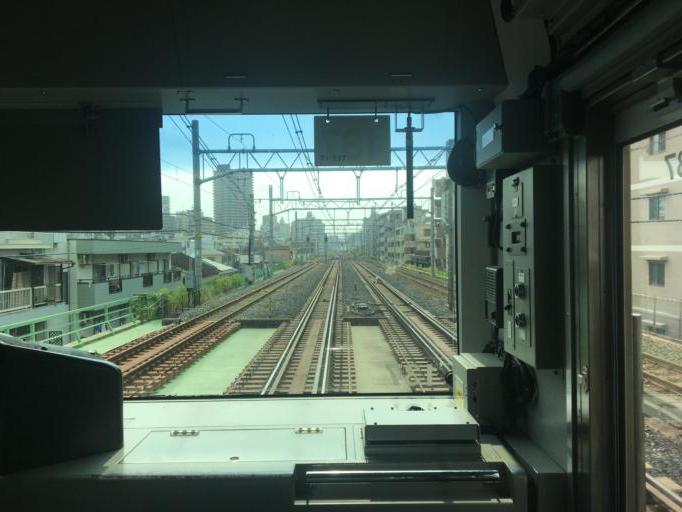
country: JP
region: Saitama
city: Soka
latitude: 35.7327
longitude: 139.7812
